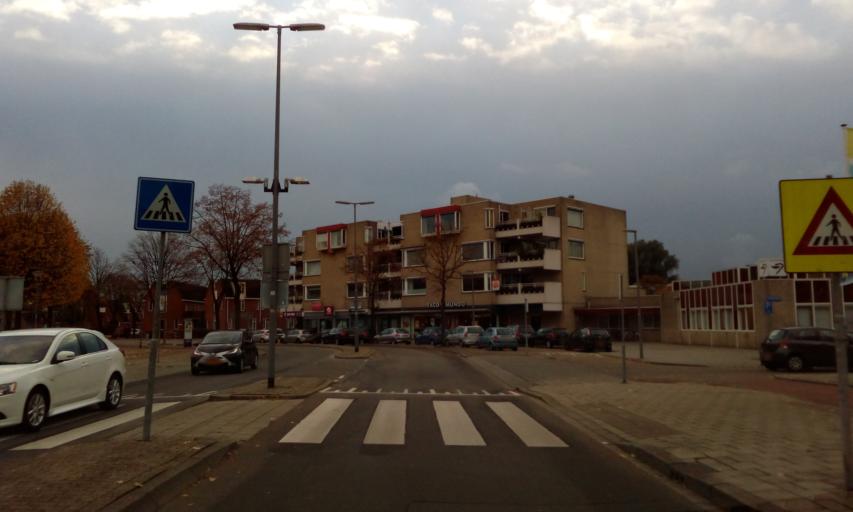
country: NL
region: South Holland
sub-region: Gemeente Capelle aan den IJssel
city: Capelle aan den IJssel
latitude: 51.9640
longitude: 4.5716
